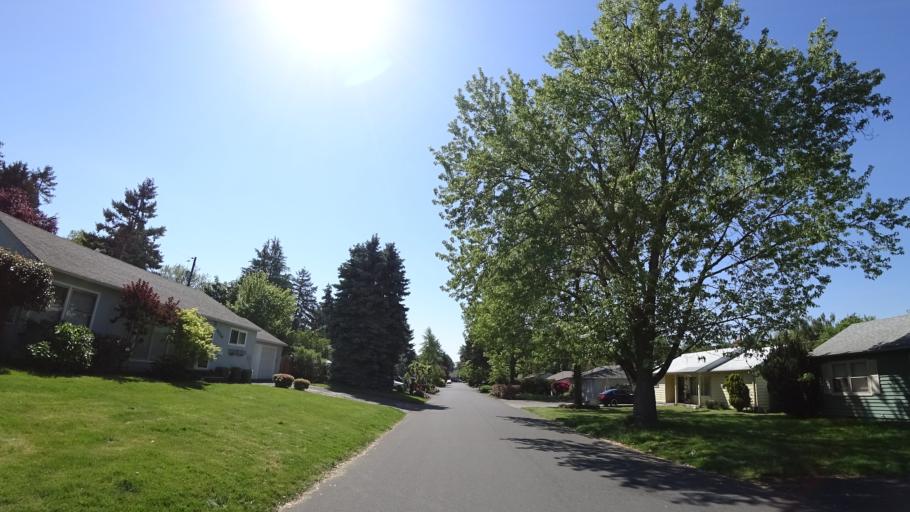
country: US
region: Oregon
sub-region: Washington County
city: Beaverton
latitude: 45.4963
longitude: -122.8024
